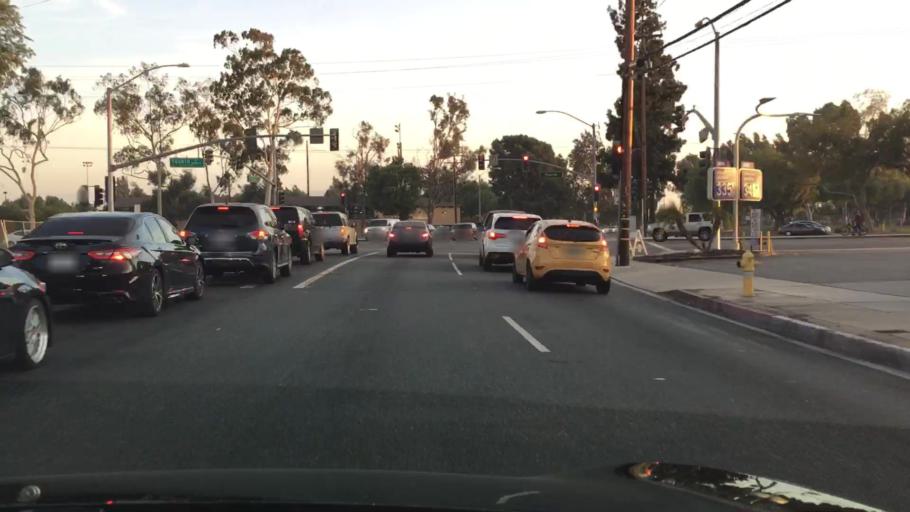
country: US
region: California
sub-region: San Bernardino County
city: Ontario
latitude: 34.0783
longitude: -117.6286
